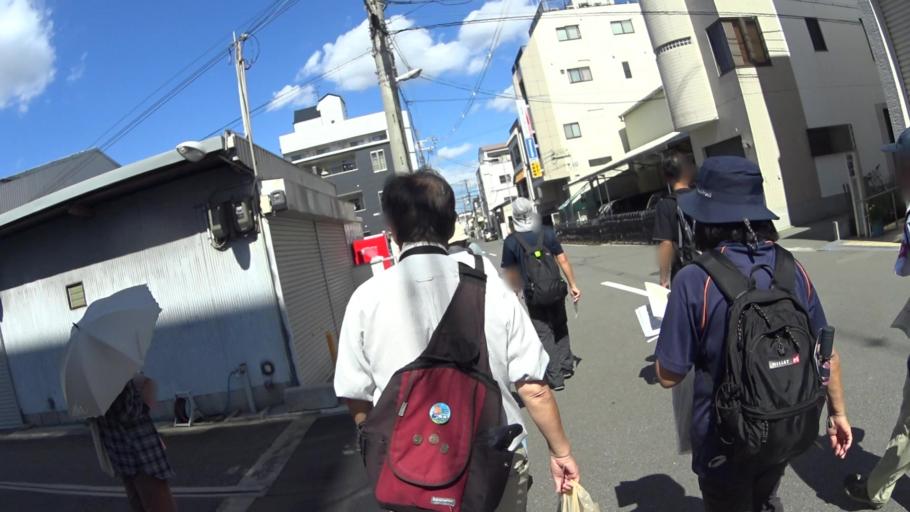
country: JP
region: Osaka
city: Yao
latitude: 34.6393
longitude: 135.5466
